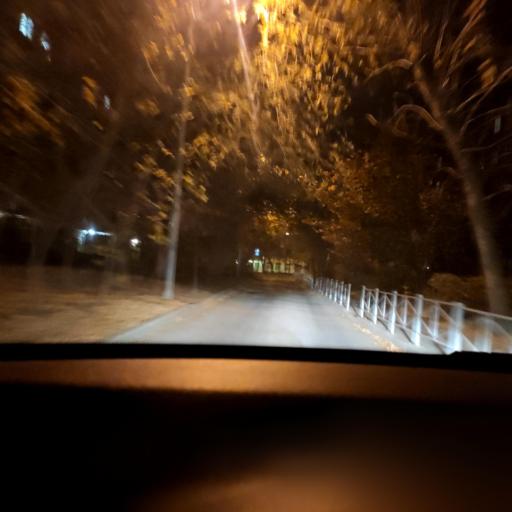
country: RU
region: Samara
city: Samara
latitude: 53.1984
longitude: 50.1623
